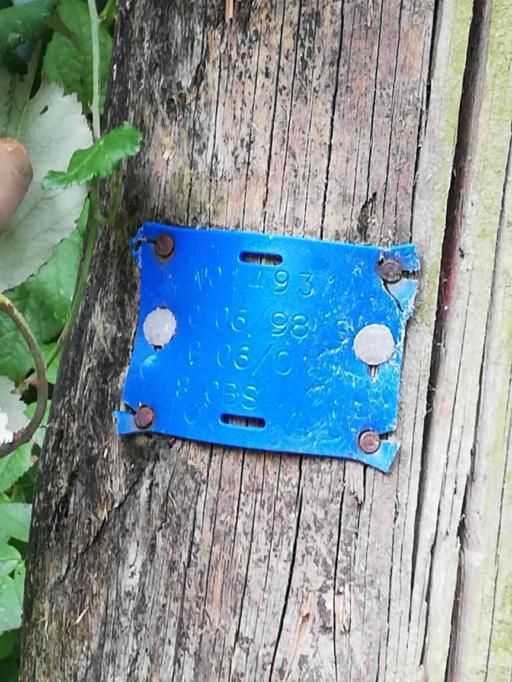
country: FR
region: Pays de la Loire
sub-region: Departement de la Vendee
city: Le Champ-Saint-Pere
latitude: 46.4993
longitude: -1.3456
